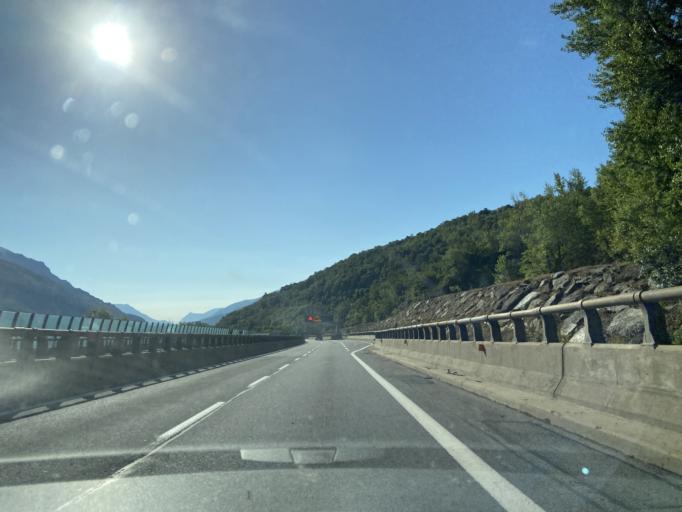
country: IT
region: Piedmont
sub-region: Provincia di Torino
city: Giaglione
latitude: 45.1463
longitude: 7.0221
